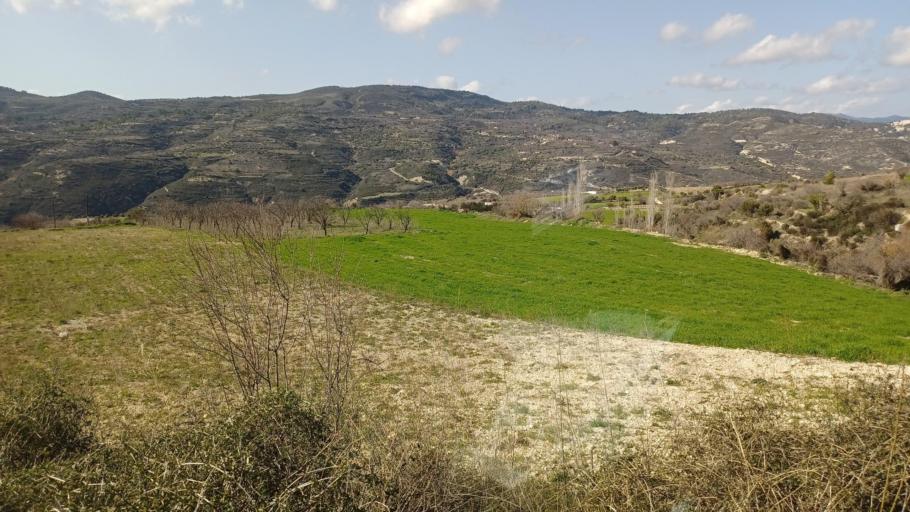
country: CY
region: Limassol
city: Pachna
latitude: 34.8444
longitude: 32.7367
